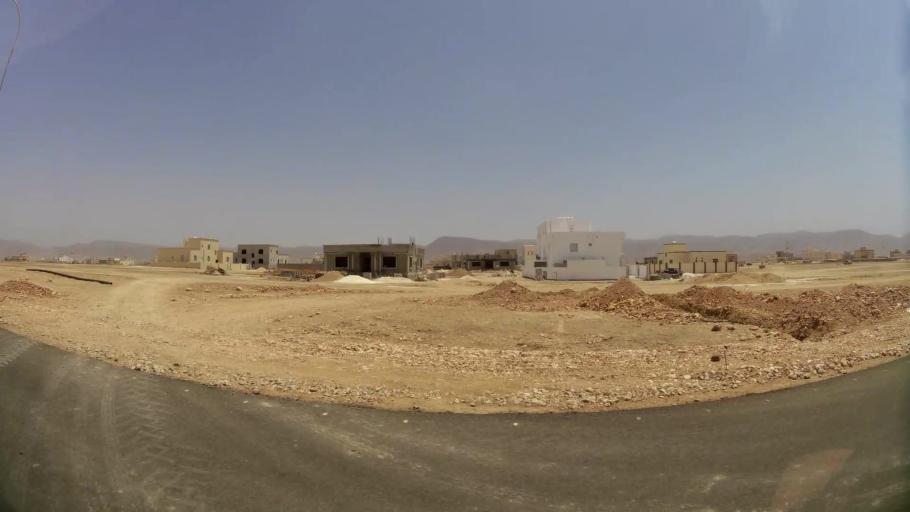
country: OM
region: Zufar
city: Salalah
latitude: 17.0978
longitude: 54.1910
